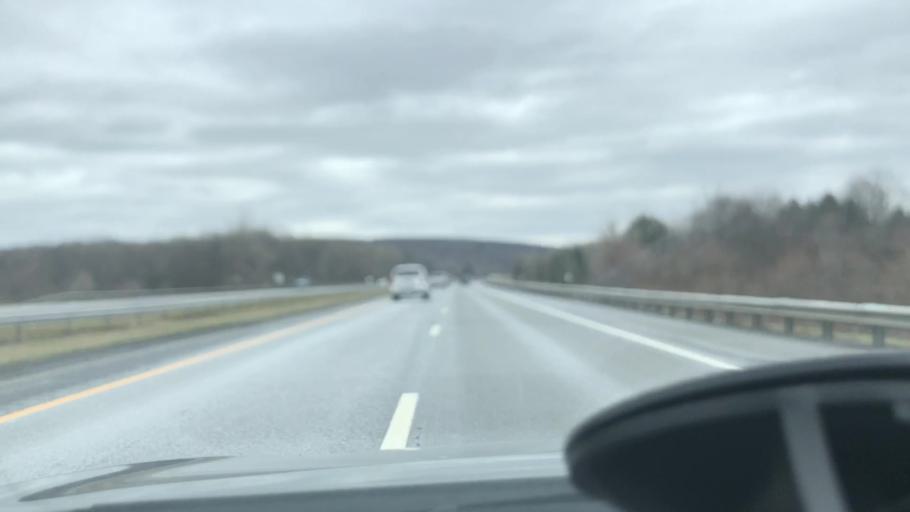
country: US
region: New York
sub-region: Herkimer County
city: Frankfort
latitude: 43.0605
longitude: -75.0757
